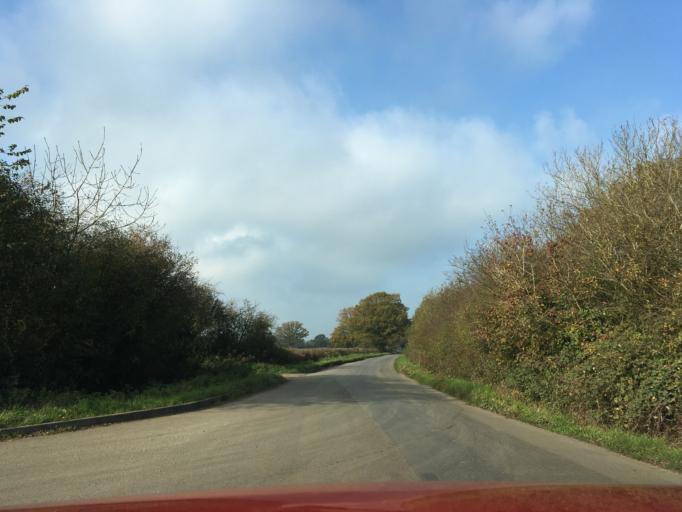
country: GB
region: England
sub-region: South Gloucestershire
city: Chipping Sodbury
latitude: 51.5646
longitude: -2.3818
